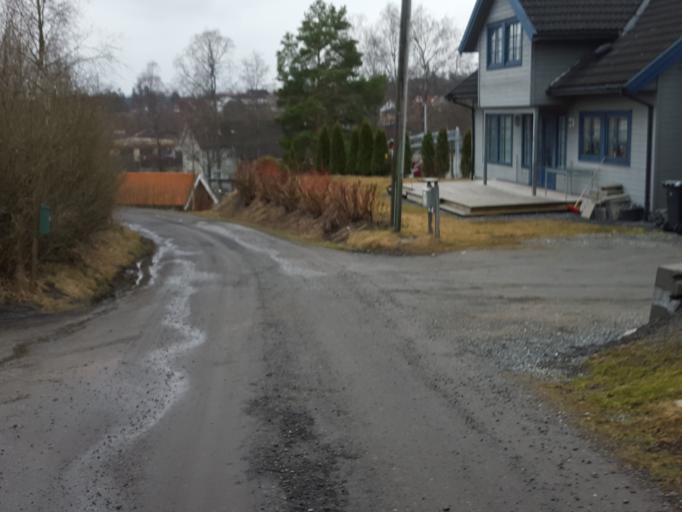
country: NO
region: Akershus
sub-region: Ski
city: Ski
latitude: 59.6840
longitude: 10.8919
